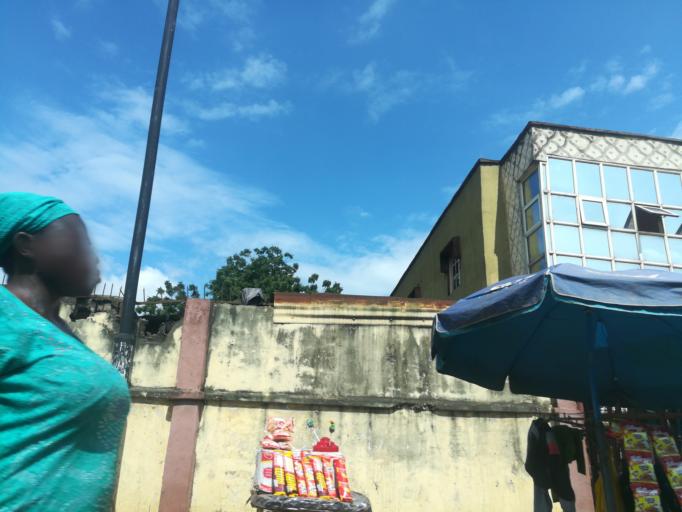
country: NG
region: Lagos
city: Agege
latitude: 6.6250
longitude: 3.3248
